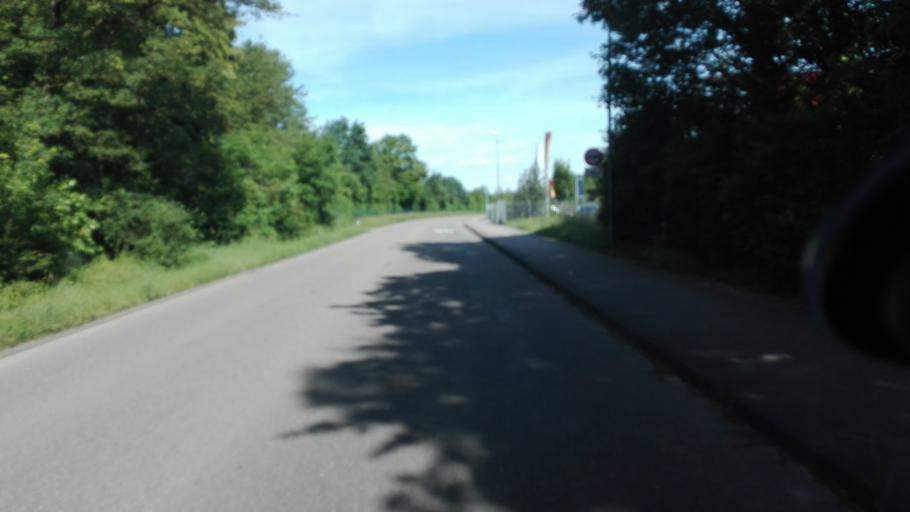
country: DE
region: Baden-Wuerttemberg
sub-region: Karlsruhe Region
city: Bruchsal
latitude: 49.1189
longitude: 8.5641
